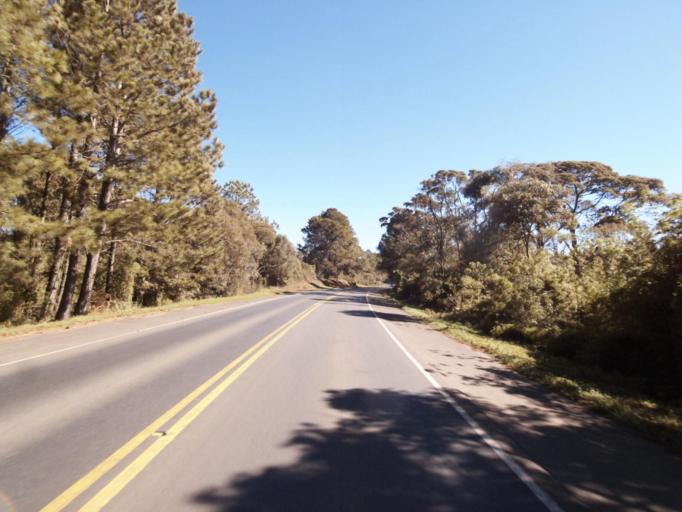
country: BR
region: Santa Catarina
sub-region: Joacaba
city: Joacaba
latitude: -26.9761
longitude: -51.7739
